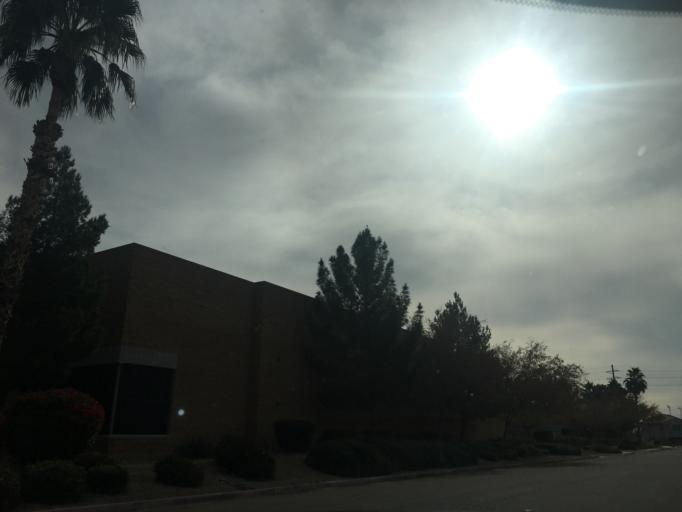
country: US
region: Arizona
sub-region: Maricopa County
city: San Carlos
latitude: 33.3658
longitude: -111.8223
